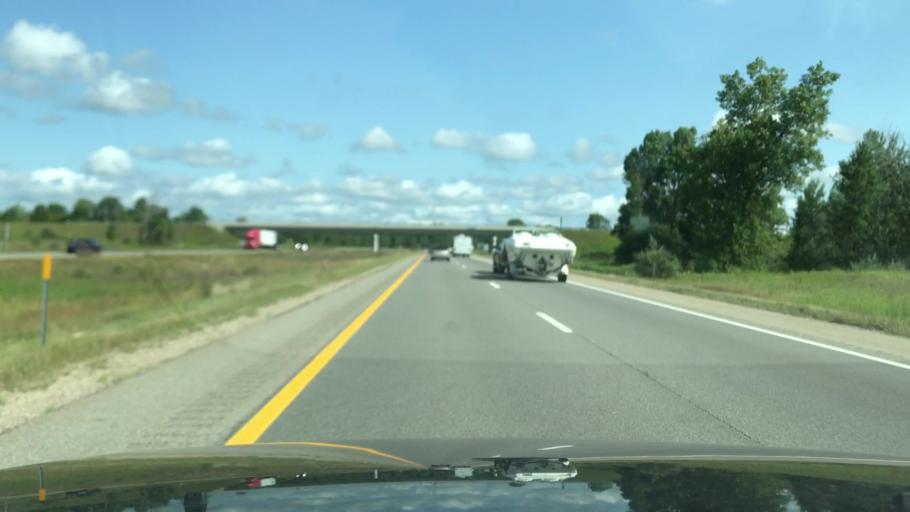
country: US
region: Michigan
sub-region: Kent County
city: Cedar Springs
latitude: 43.2919
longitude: -85.5420
